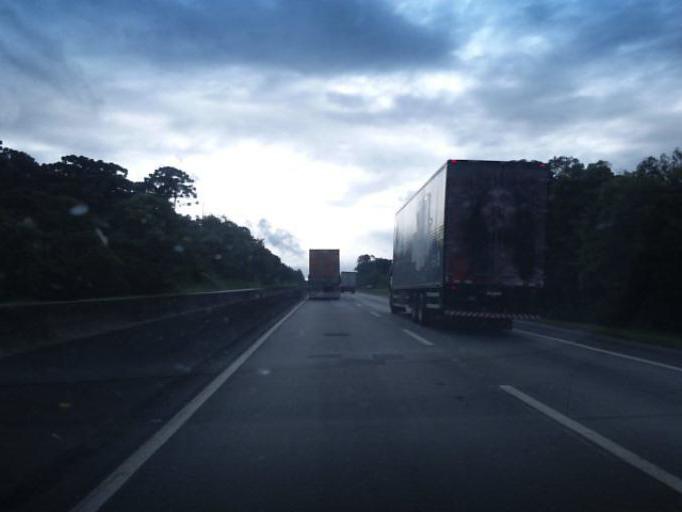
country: BR
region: Parana
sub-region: Campina Grande Do Sul
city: Campina Grande do Sul
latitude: -25.3053
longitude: -48.9721
